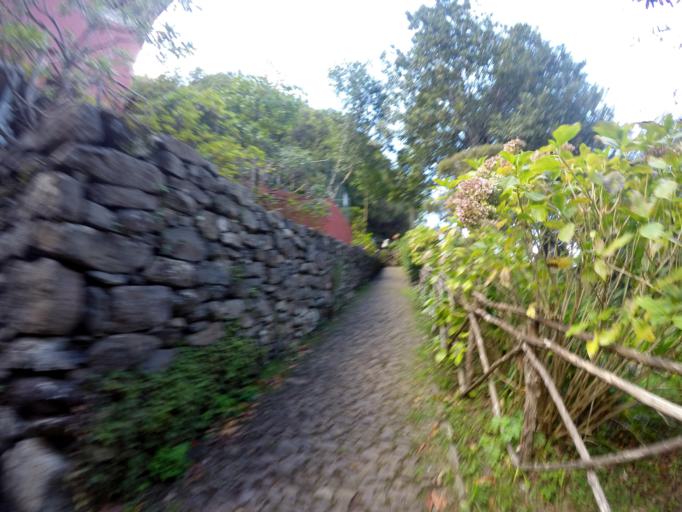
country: PT
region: Madeira
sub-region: Santana
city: Santana
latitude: 32.7350
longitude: -16.8862
